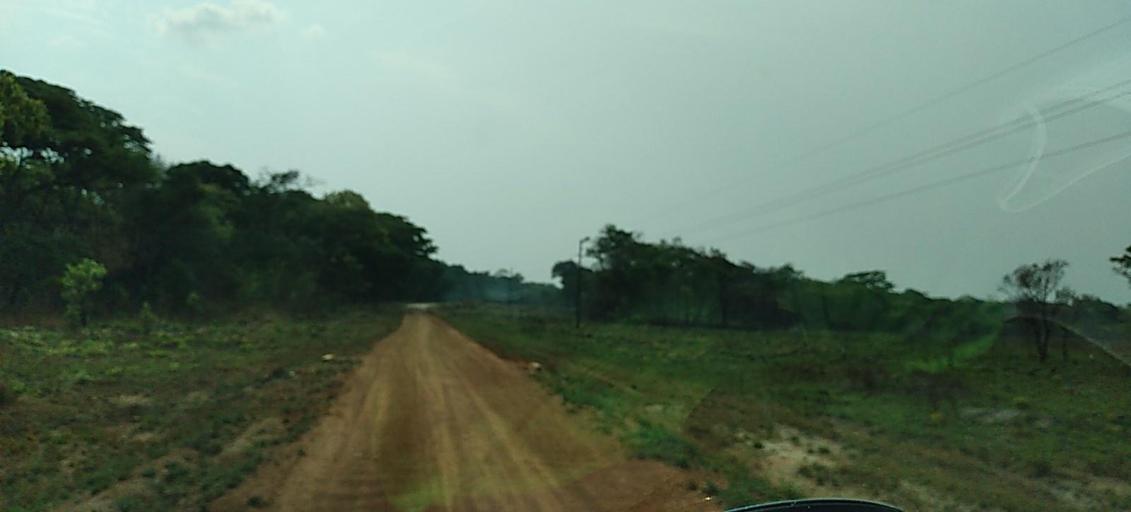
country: ZM
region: North-Western
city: Solwezi
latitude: -12.6950
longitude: 26.4056
